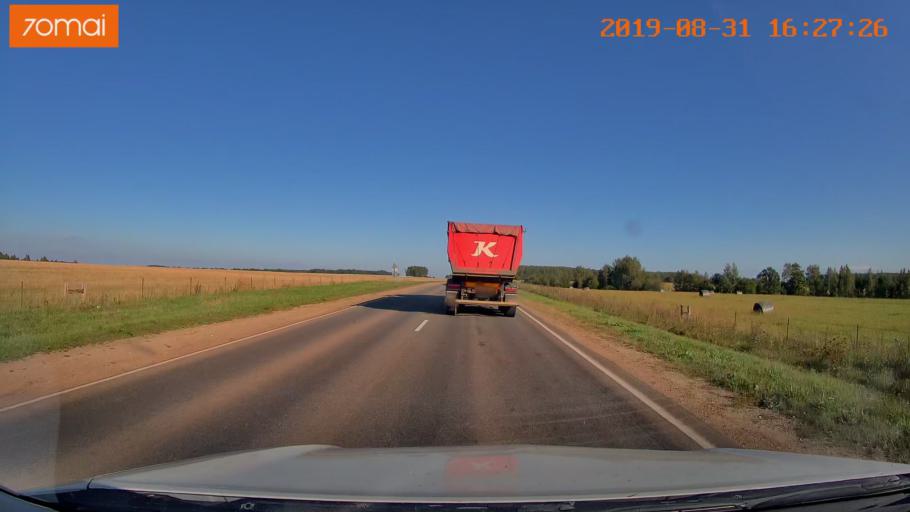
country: RU
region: Kaluga
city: Babynino
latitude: 54.5139
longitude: 35.7575
